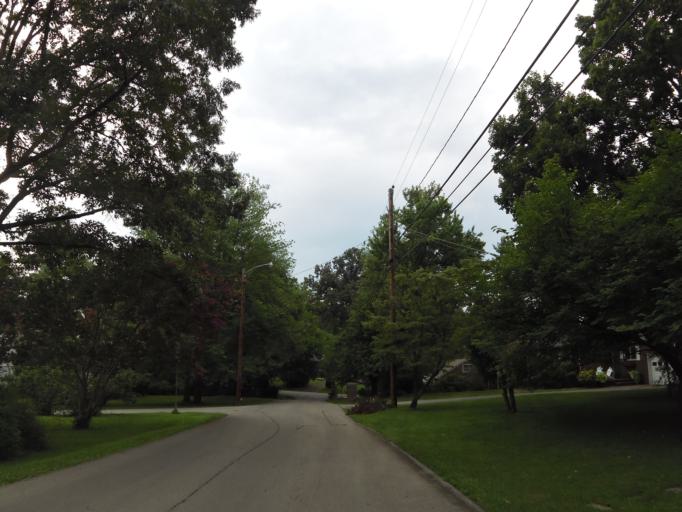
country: US
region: Tennessee
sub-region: Blount County
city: Maryville
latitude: 35.7462
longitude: -83.9865
